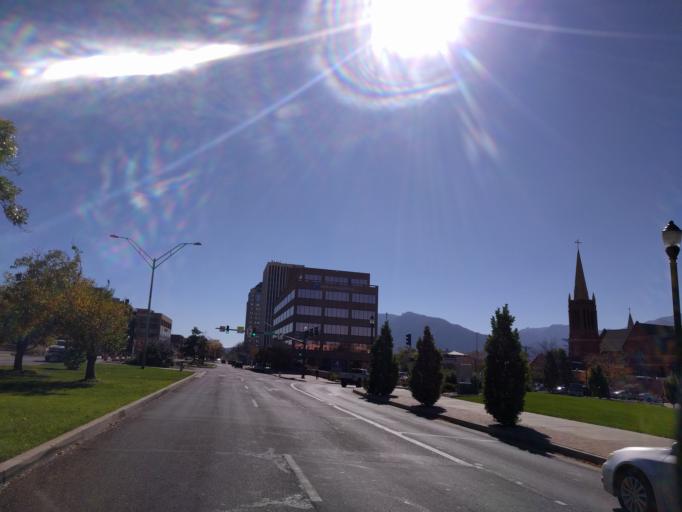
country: US
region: Colorado
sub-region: El Paso County
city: Colorado Springs
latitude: 38.8374
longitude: -104.8253
